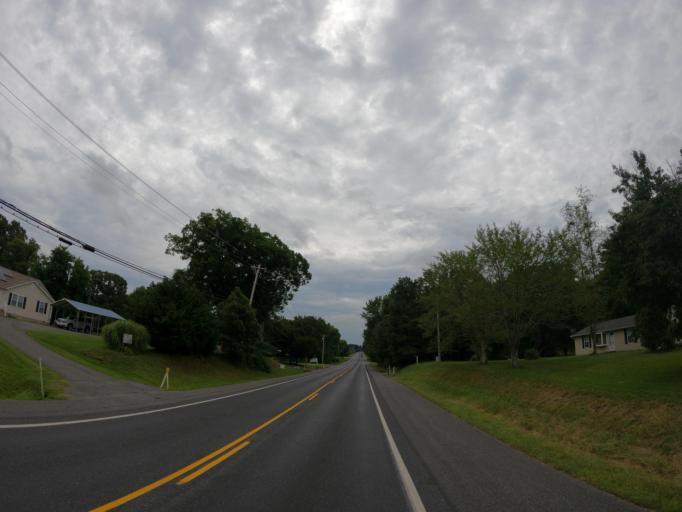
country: US
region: Maryland
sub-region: Saint Mary's County
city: Lexington Park
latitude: 38.2225
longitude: -76.5175
